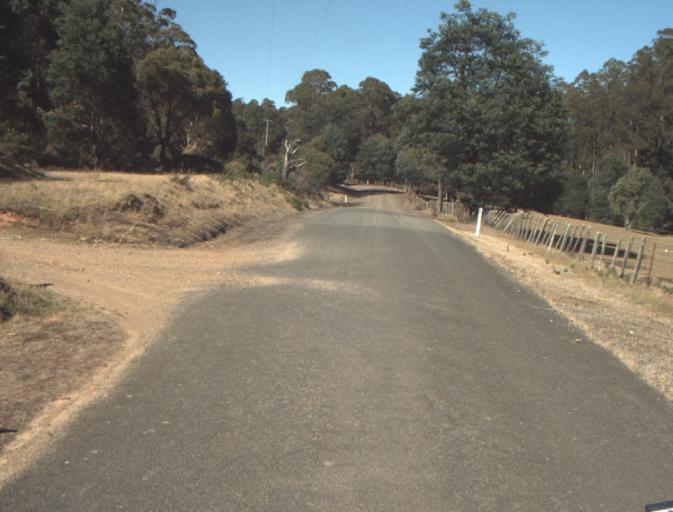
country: AU
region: Tasmania
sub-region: Launceston
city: Newstead
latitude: -41.2978
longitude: 147.3360
